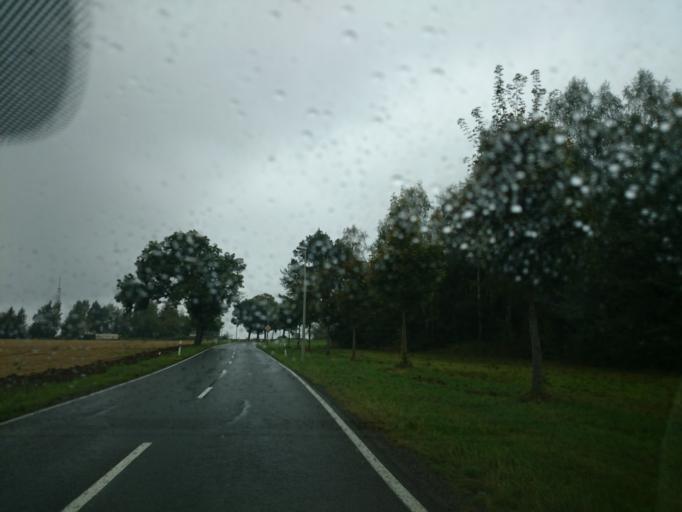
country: DE
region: Saxony
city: Brand-Erbisdorf
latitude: 50.8794
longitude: 13.3383
